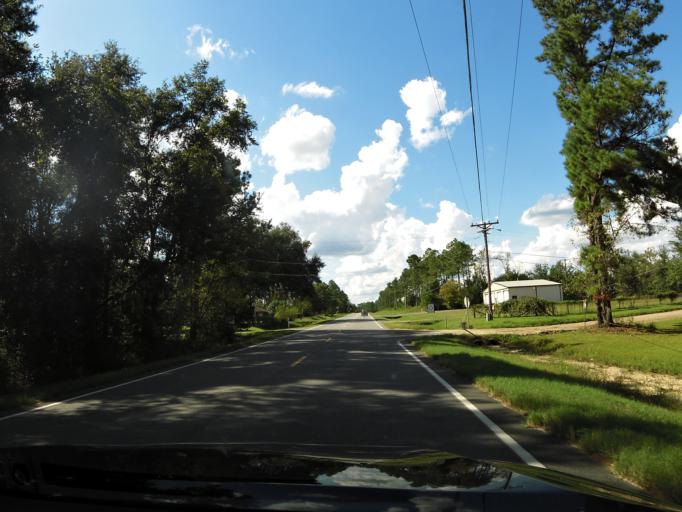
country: US
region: Georgia
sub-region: Lowndes County
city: Valdosta
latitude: 30.8016
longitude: -83.1994
